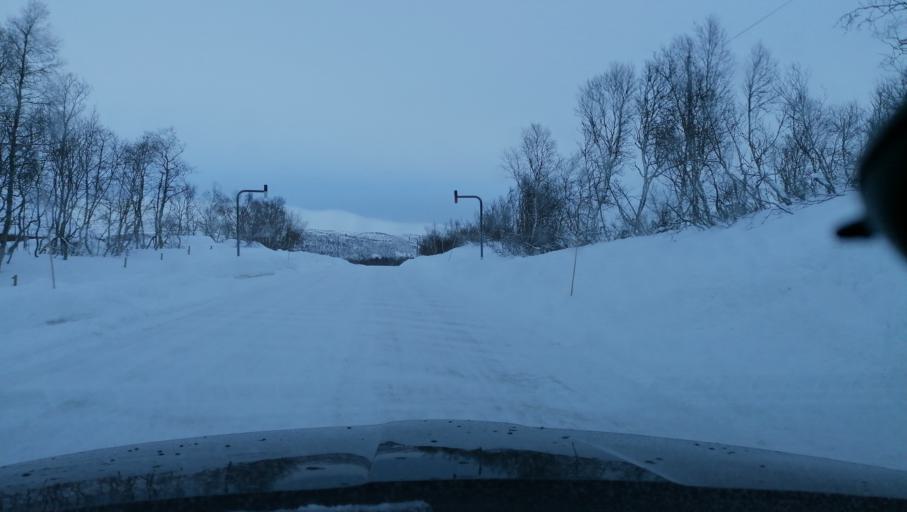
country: NO
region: Aust-Agder
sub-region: Bykle
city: Hovden
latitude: 59.6424
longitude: 7.4578
